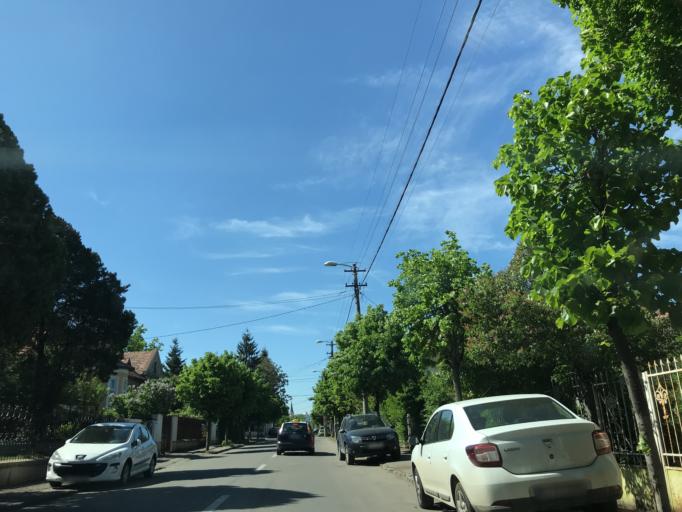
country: RO
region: Cluj
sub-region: Municipiul Cluj-Napoca
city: Cluj-Napoca
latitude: 46.7643
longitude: 23.6019
